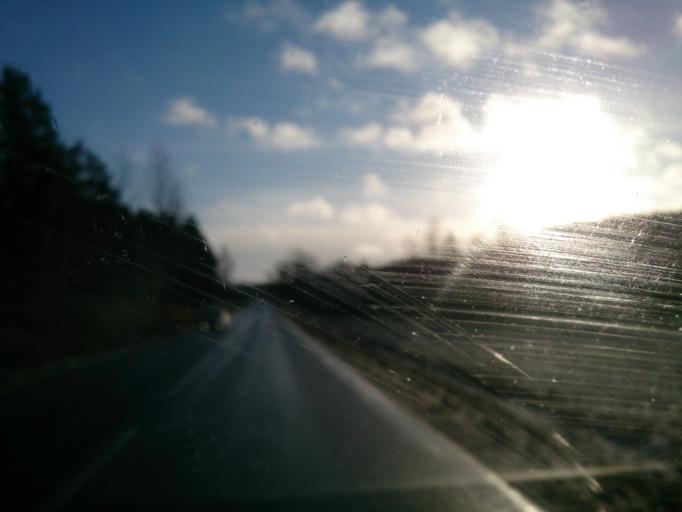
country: SE
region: OEstergoetland
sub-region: Atvidabergs Kommun
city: Atvidaberg
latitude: 58.2825
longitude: 15.9022
